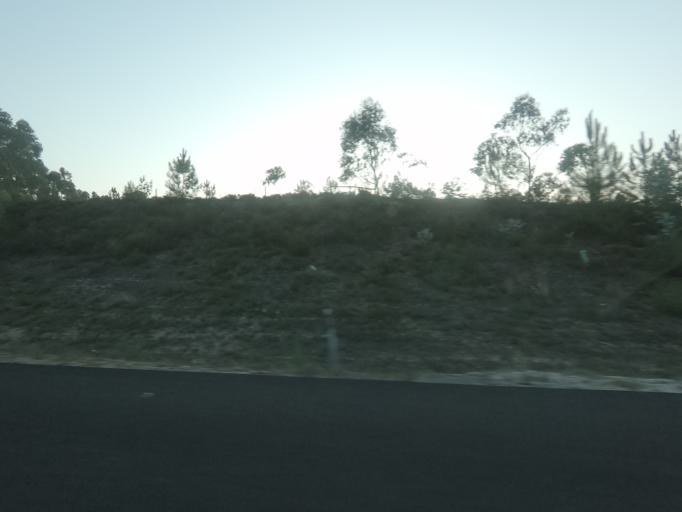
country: PT
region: Leiria
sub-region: Pombal
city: Pombal
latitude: 39.8707
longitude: -8.7038
